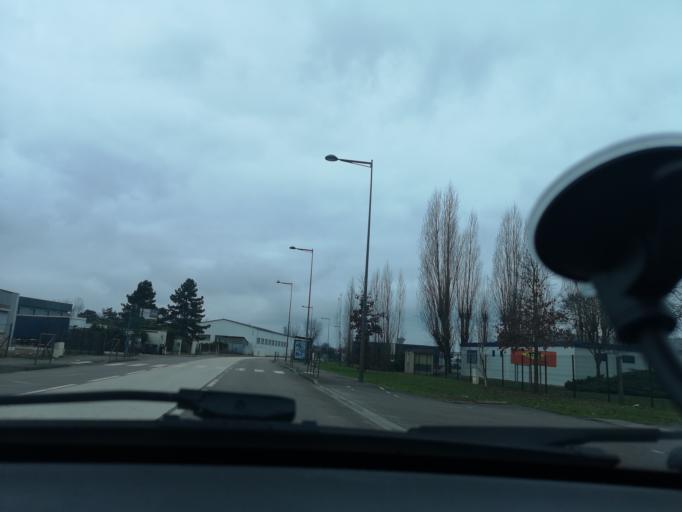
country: FR
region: Bourgogne
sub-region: Departement de Saone-et-Loire
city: Virey-le-Grand
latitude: 46.8204
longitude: 4.8625
